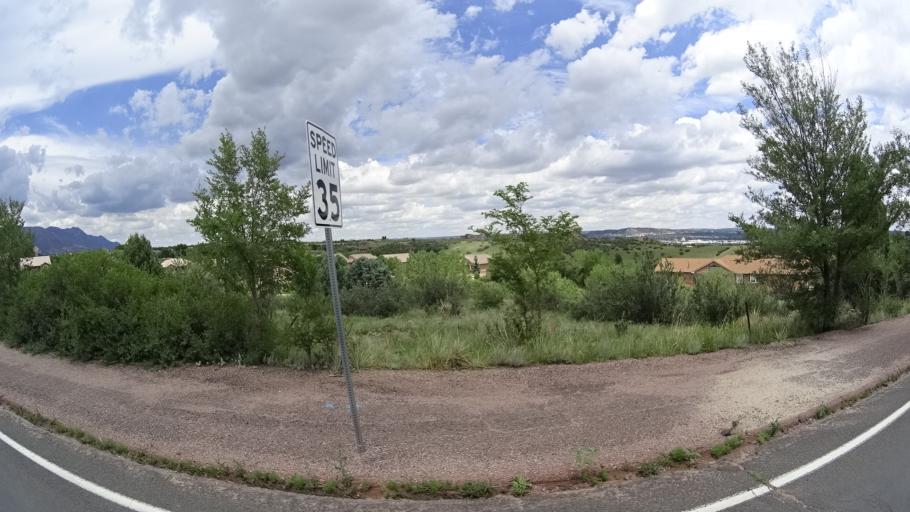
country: US
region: Colorado
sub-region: El Paso County
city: Colorado Springs
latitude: 38.8637
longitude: -104.8527
